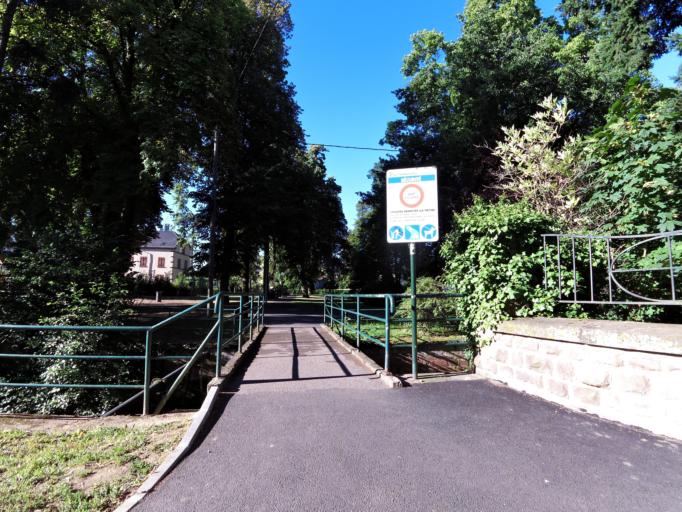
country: FR
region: Alsace
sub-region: Departement du Bas-Rhin
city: Wissembourg
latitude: 49.0340
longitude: 7.9471
